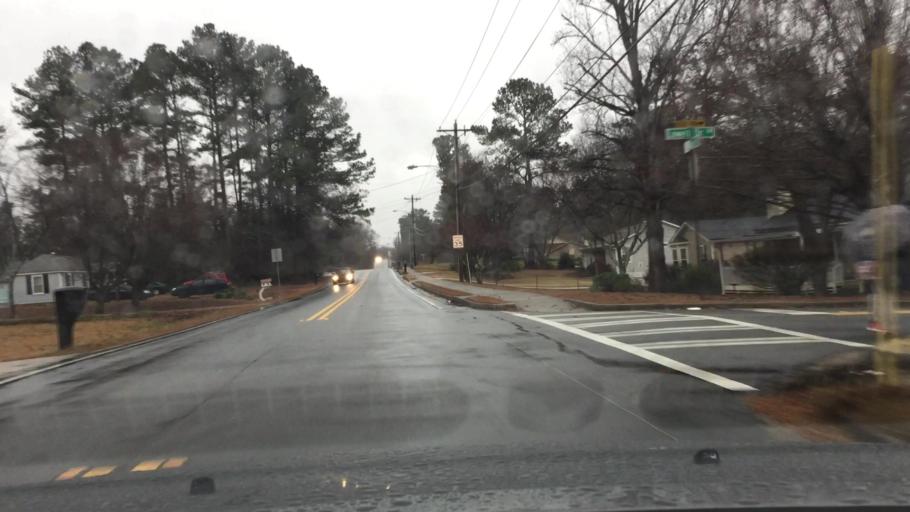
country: US
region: Georgia
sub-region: Cobb County
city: Fair Oaks
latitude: 33.9157
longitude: -84.5761
